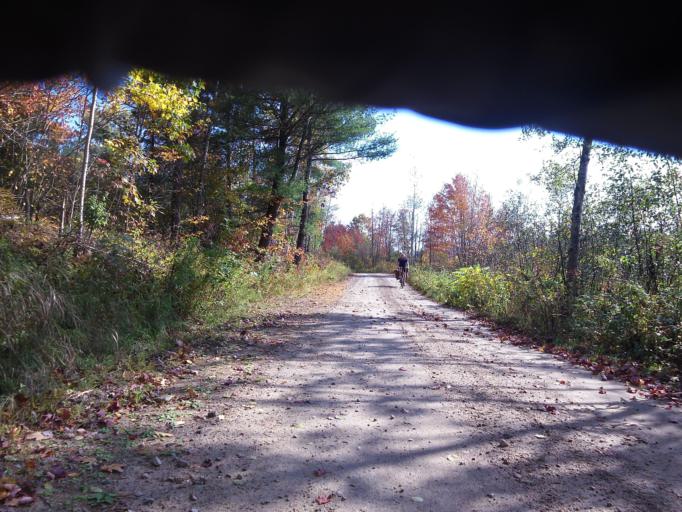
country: CA
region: Ontario
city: Petawawa
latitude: 45.7995
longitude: -77.3168
